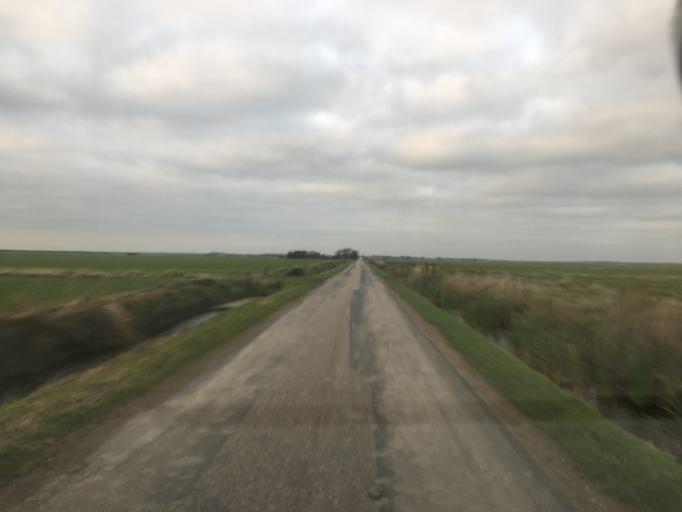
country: DE
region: Schleswig-Holstein
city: Klanxbull
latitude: 54.9322
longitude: 8.6818
